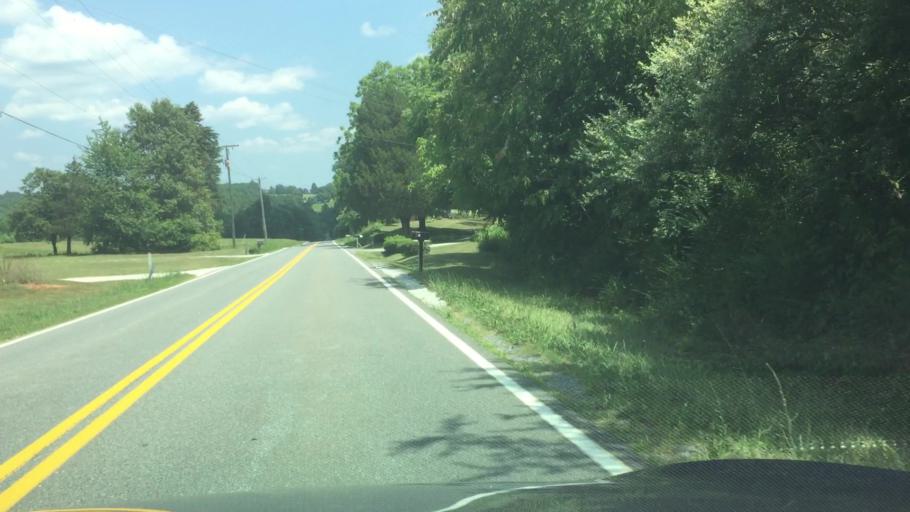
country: US
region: Virginia
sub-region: Appomattox County
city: Appomattox
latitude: 37.3421
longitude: -78.8974
